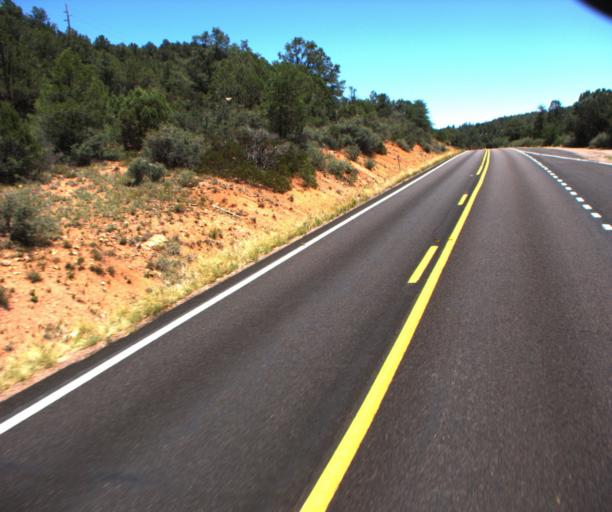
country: US
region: Arizona
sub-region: Gila County
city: Payson
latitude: 34.2892
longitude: -111.3439
